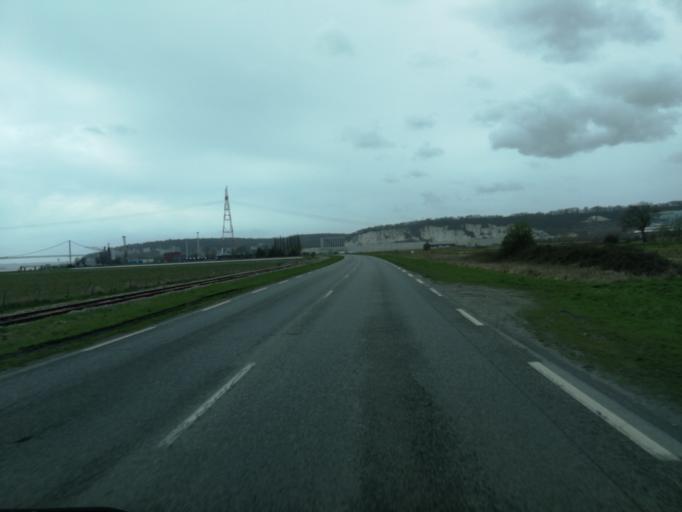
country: FR
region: Haute-Normandie
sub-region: Departement de la Seine-Maritime
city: Saint-Nicolas-de-la-Taille
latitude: 49.4895
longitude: 0.4981
